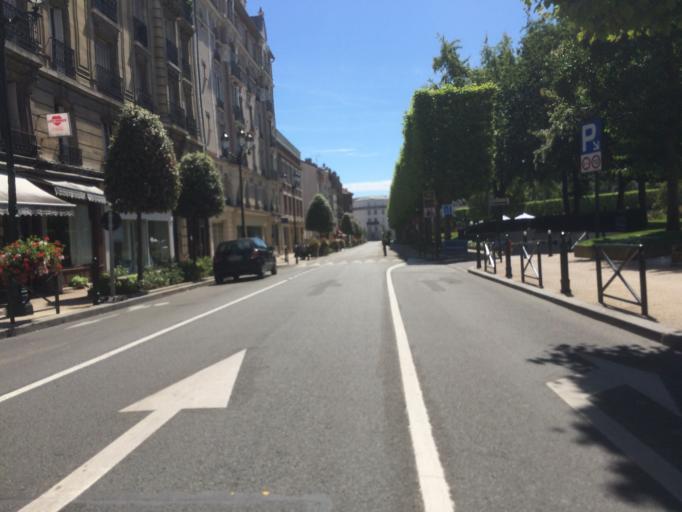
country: FR
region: Ile-de-France
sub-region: Departement des Hauts-de-Seine
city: Puteaux
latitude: 48.8845
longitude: 2.2393
